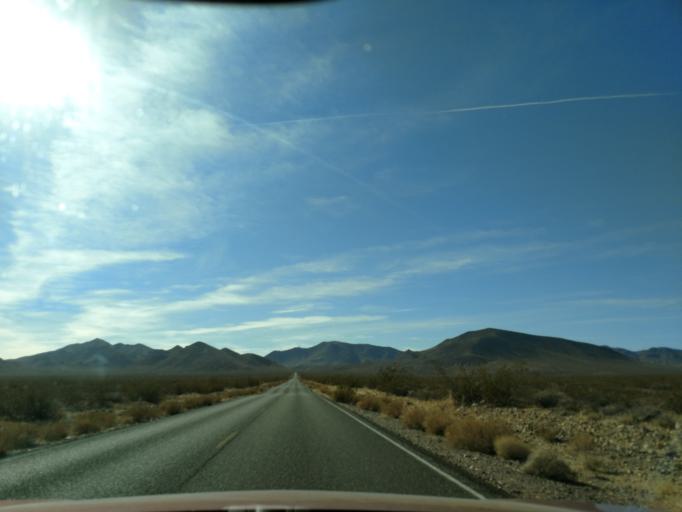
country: US
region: Nevada
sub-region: Nye County
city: Beatty
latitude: 36.8256
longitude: -116.8889
